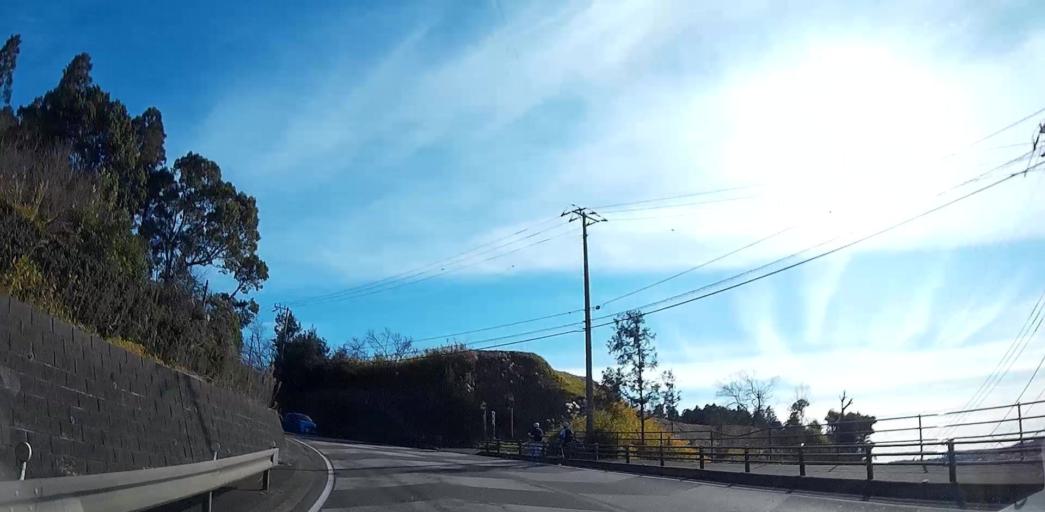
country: JP
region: Chiba
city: Yokaichiba
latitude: 35.7400
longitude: 140.4787
